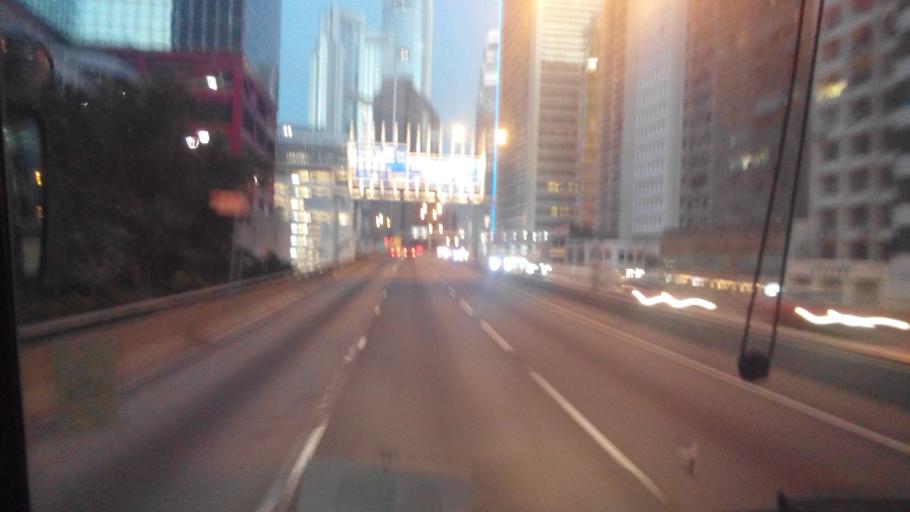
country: HK
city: Hong Kong
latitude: 22.2878
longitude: 114.1512
